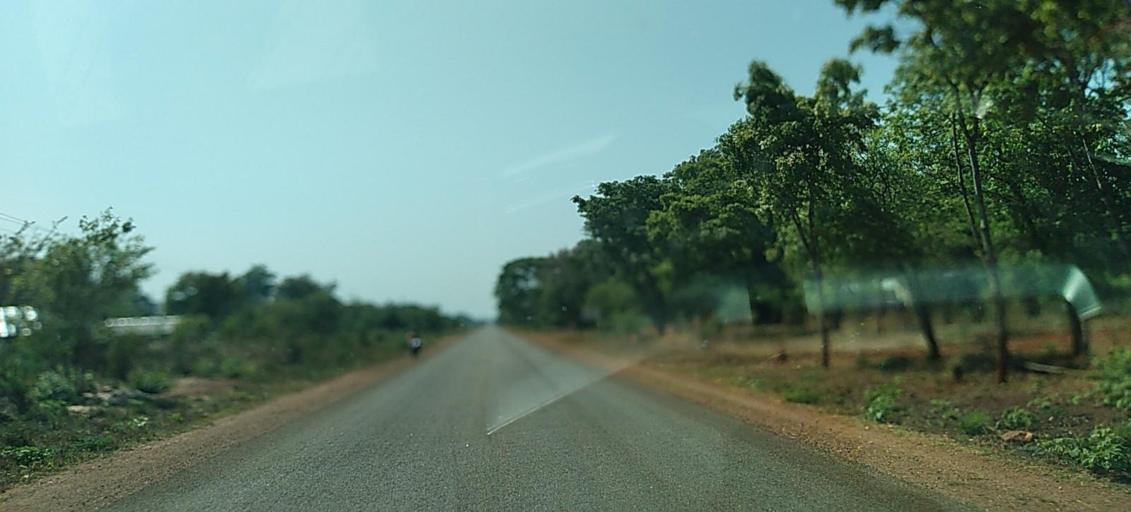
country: ZM
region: North-Western
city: Solwezi
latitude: -12.1240
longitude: 25.5184
